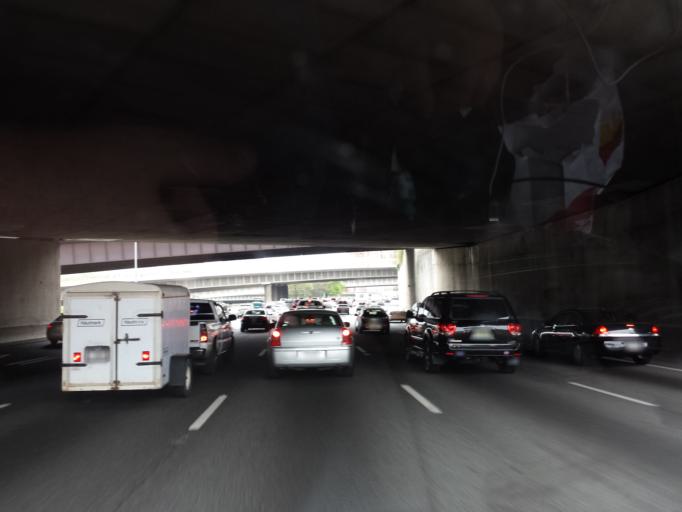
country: US
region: Georgia
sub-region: Fulton County
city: Atlanta
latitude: 33.7666
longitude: -84.3873
